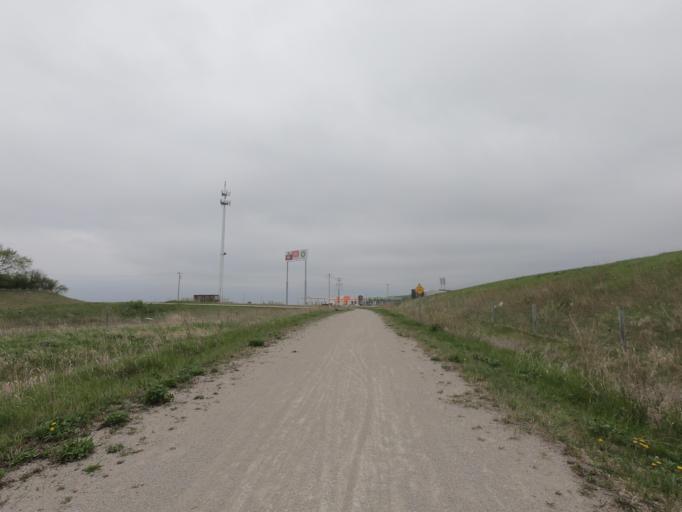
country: US
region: Wisconsin
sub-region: Jefferson County
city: Jefferson
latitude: 43.0329
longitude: -88.8038
